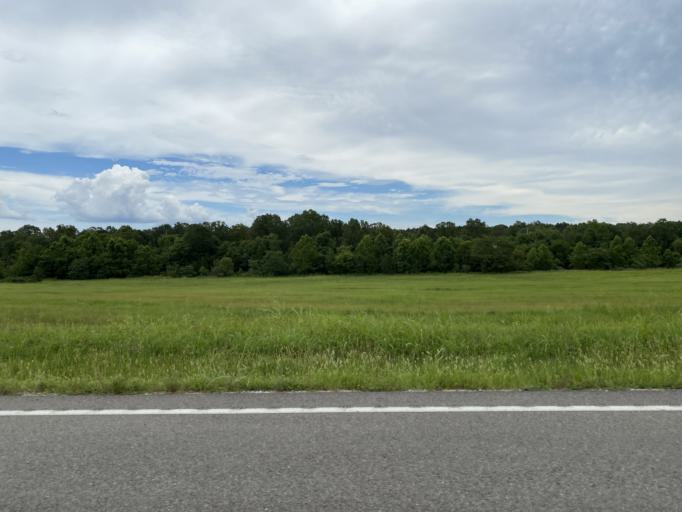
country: US
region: Arkansas
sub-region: Fulton County
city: Salem
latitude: 36.3589
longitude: -91.8347
